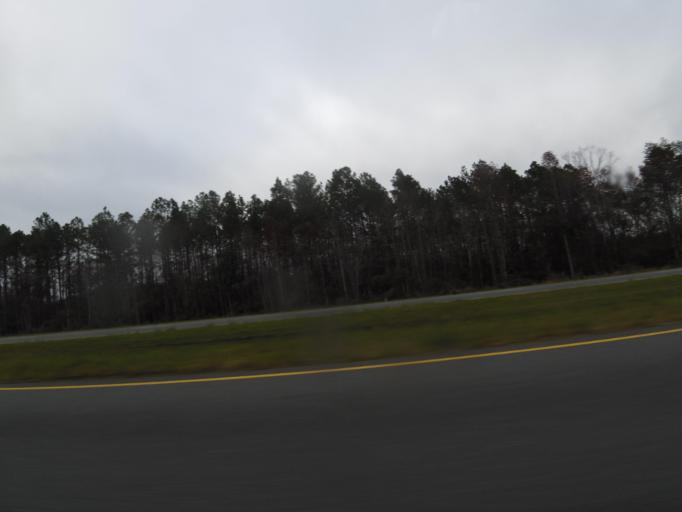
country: US
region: Georgia
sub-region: Charlton County
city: Folkston
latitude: 30.8827
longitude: -82.0382
